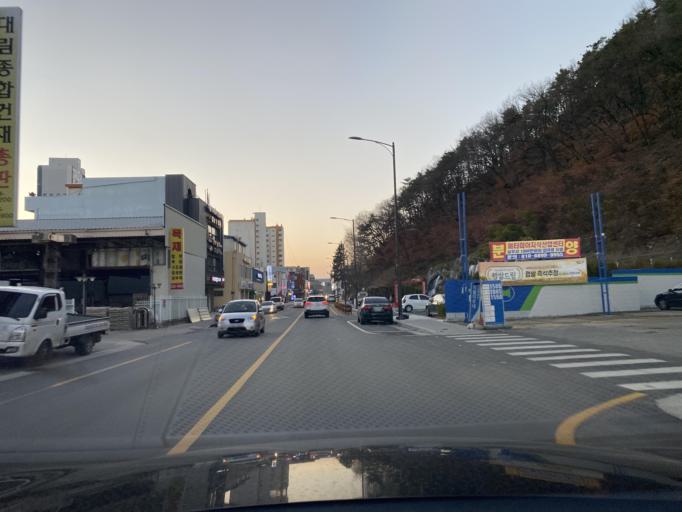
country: KR
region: Chungcheongnam-do
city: Yesan
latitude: 36.6786
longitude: 126.8402
